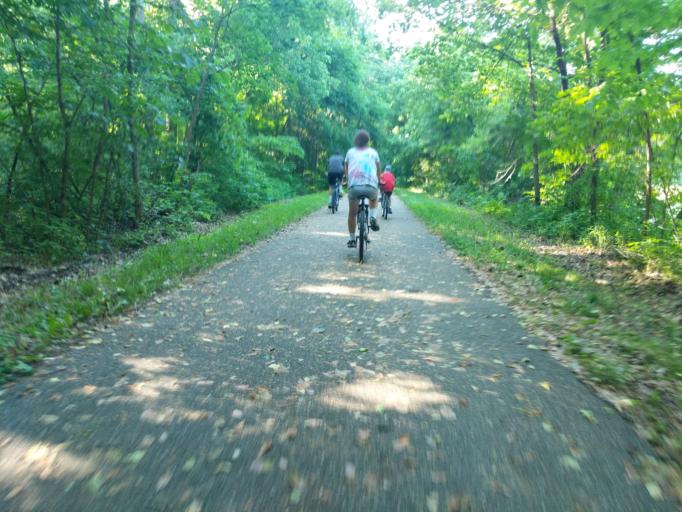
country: US
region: Ohio
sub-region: Athens County
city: Nelsonville
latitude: 39.4226
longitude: -82.1956
